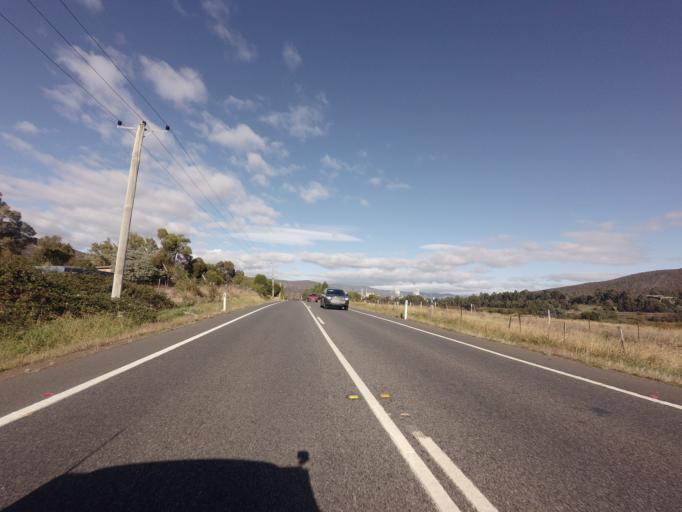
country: AU
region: Tasmania
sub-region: Derwent Valley
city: New Norfolk
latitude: -42.7764
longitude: 147.1164
